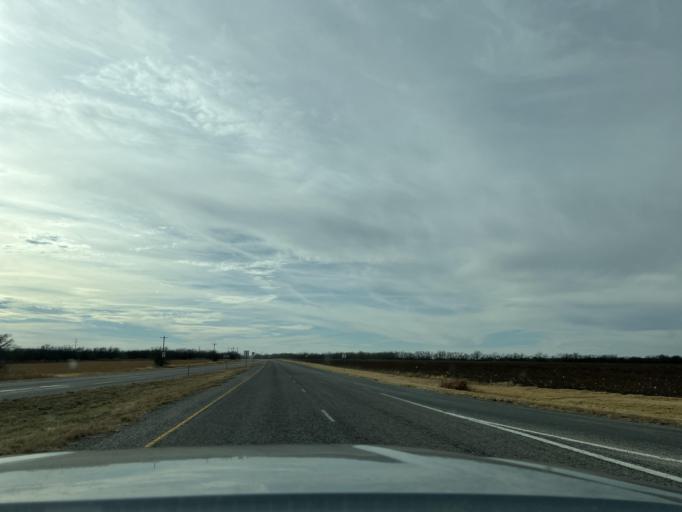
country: US
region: Texas
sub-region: Jones County
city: Stamford
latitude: 32.7665
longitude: -99.5909
